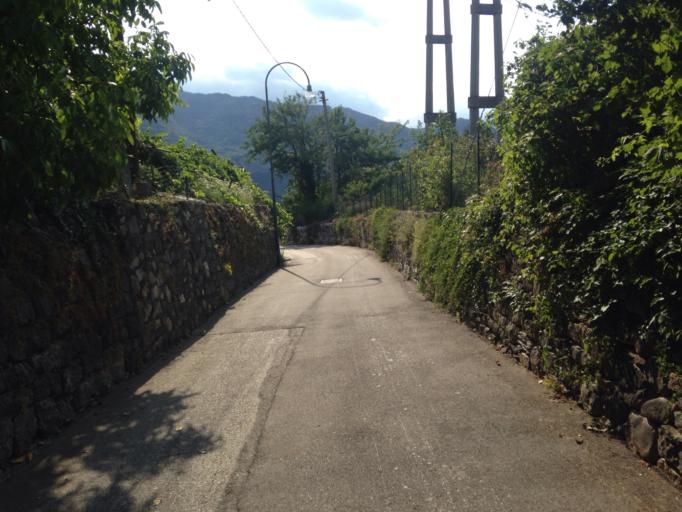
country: IT
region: Trentino-Alto Adige
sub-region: Provincia di Trento
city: Povo
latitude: 46.0664
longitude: 11.1437
